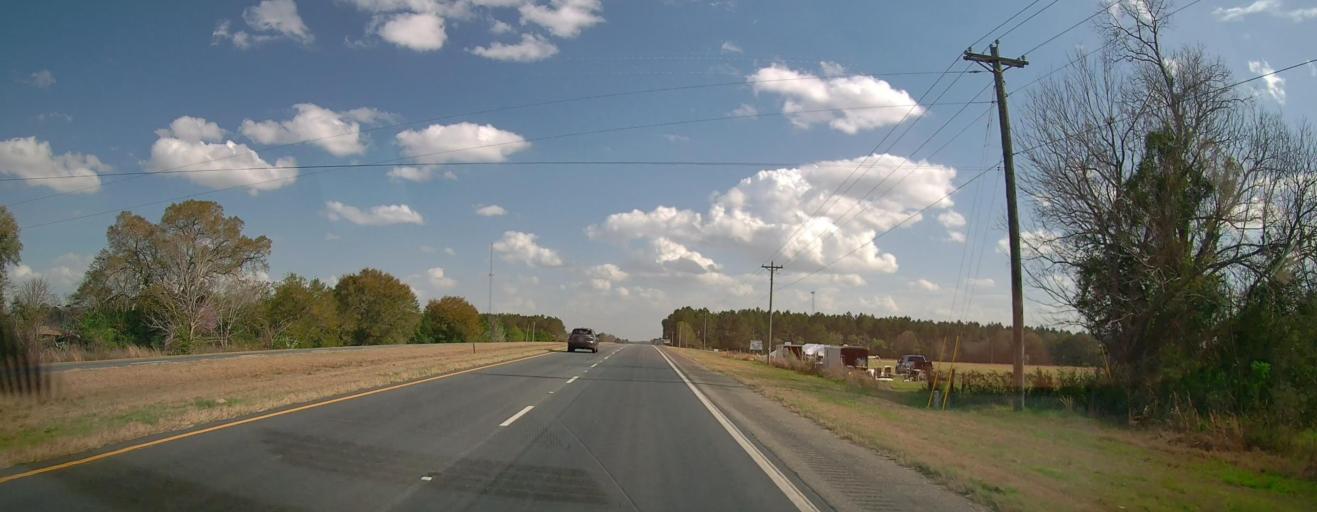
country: US
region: Georgia
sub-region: Dodge County
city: Eastman
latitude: 32.1497
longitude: -83.1395
